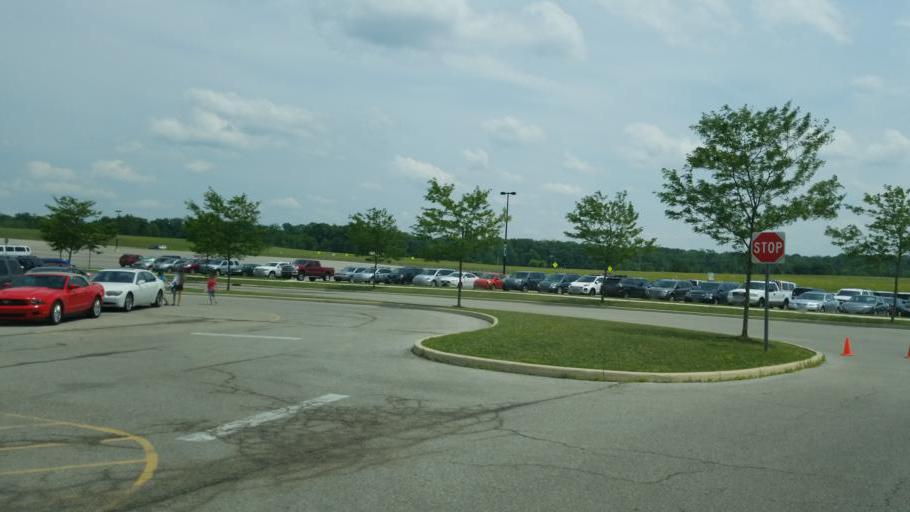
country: US
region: Ohio
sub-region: Delaware County
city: Powell
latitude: 40.1537
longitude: -83.1157
